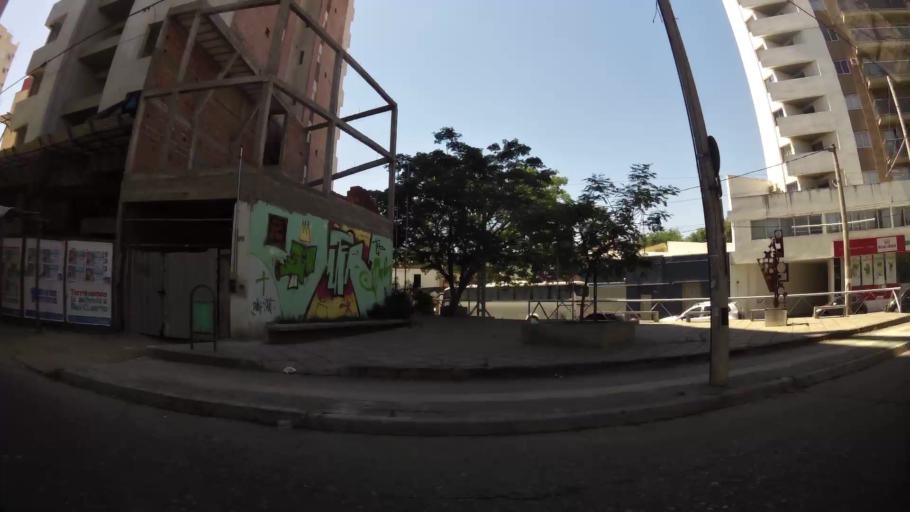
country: AR
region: Cordoba
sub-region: Departamento de Capital
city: Cordoba
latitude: -31.4268
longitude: -64.1943
